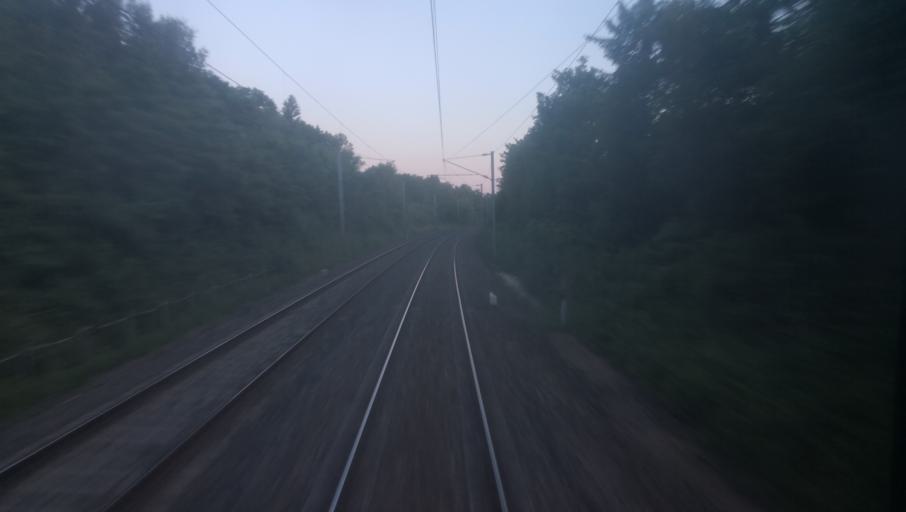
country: FR
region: Bourgogne
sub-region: Departement de la Nievre
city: Cosne-Cours-sur-Loire
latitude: 47.4397
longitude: 2.9336
